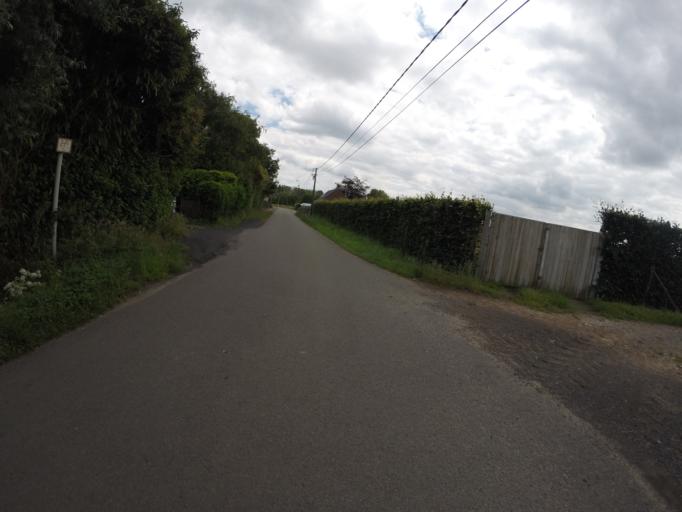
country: BE
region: Flanders
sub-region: Provincie Oost-Vlaanderen
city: Aalter
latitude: 51.1225
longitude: 3.4411
